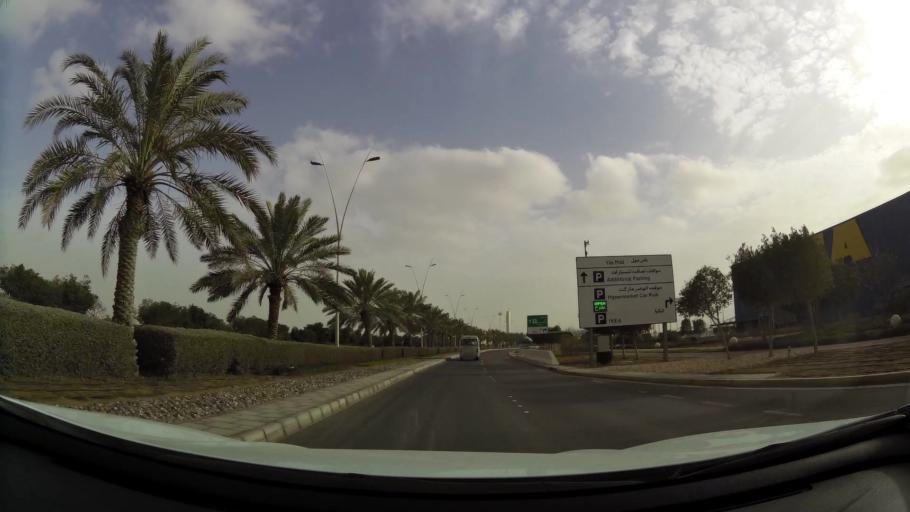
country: AE
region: Abu Dhabi
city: Abu Dhabi
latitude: 24.4903
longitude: 54.6149
